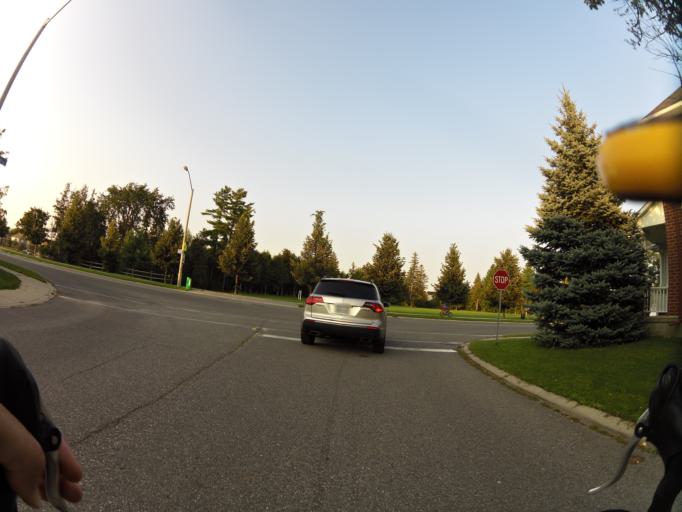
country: CA
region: Ontario
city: Bells Corners
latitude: 45.3516
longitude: -75.9433
